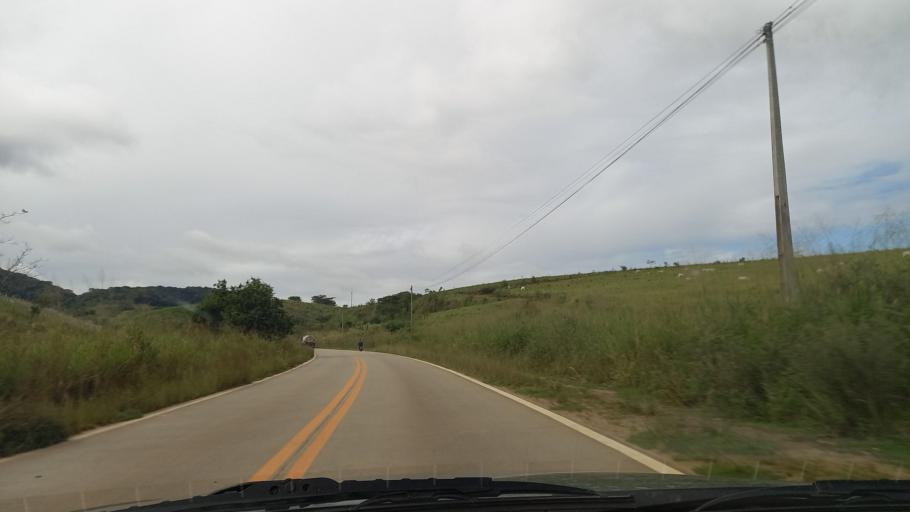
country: BR
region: Pernambuco
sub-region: Maraial
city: Maraial
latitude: -8.7577
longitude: -35.8490
